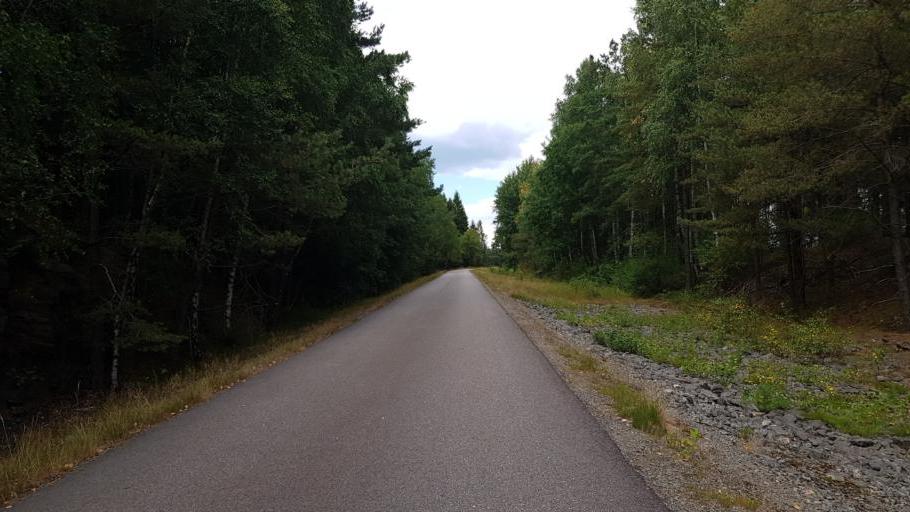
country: SE
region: Vaestra Goetaland
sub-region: Harryda Kommun
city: Molnlycke
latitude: 57.6760
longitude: 12.0845
